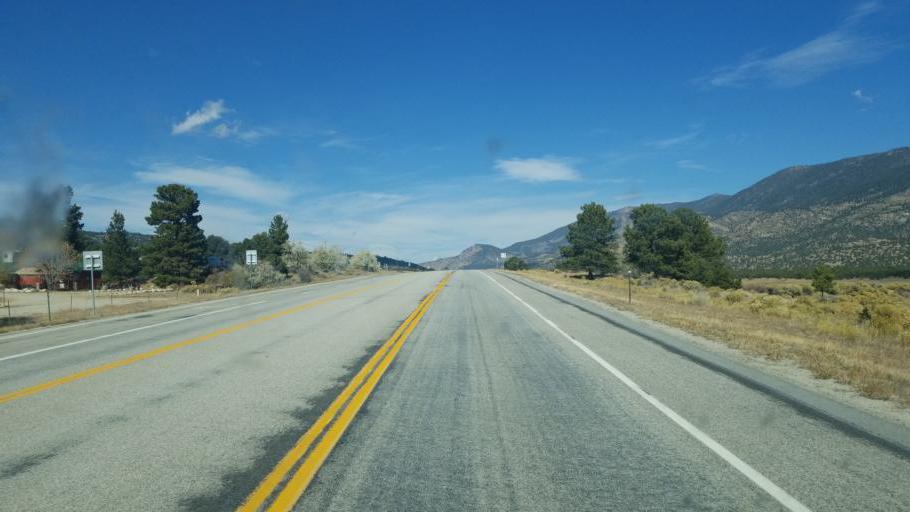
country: US
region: Colorado
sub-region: Chaffee County
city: Buena Vista
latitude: 38.9108
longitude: -106.1796
